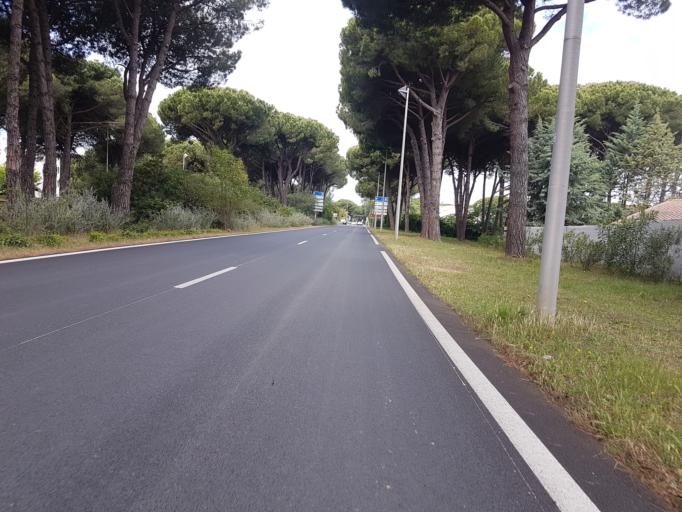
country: FR
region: Languedoc-Roussillon
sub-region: Departement de l'Herault
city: La Grande-Motte
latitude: 43.5636
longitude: 4.0894
